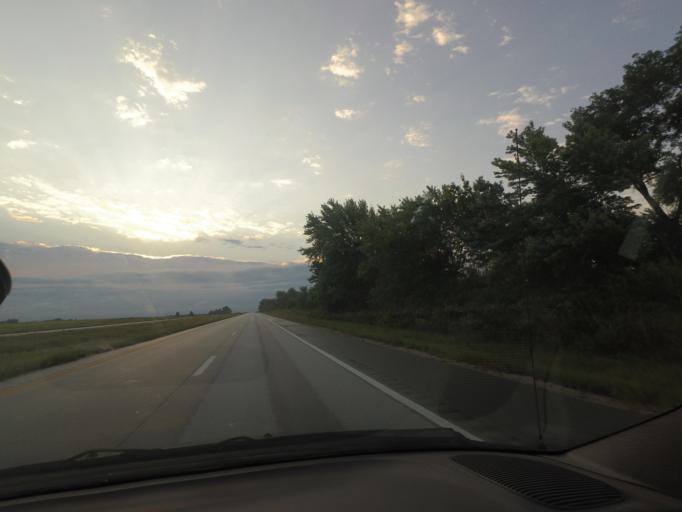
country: US
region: Missouri
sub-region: Shelby County
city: Shelbina
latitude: 39.7296
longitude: -92.1940
